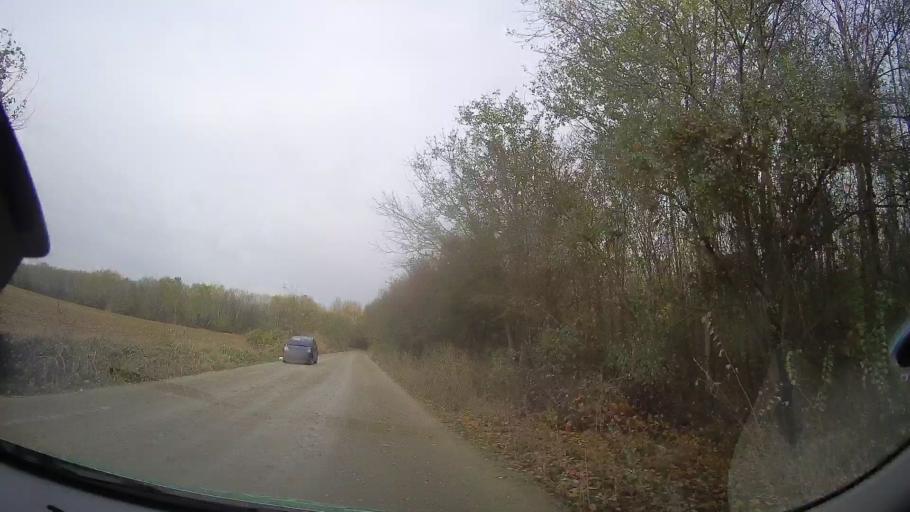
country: RO
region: Ialomita
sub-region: Comuna Fierbinti-Targ
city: Fierbinti-Targ
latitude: 44.6804
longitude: 26.3477
